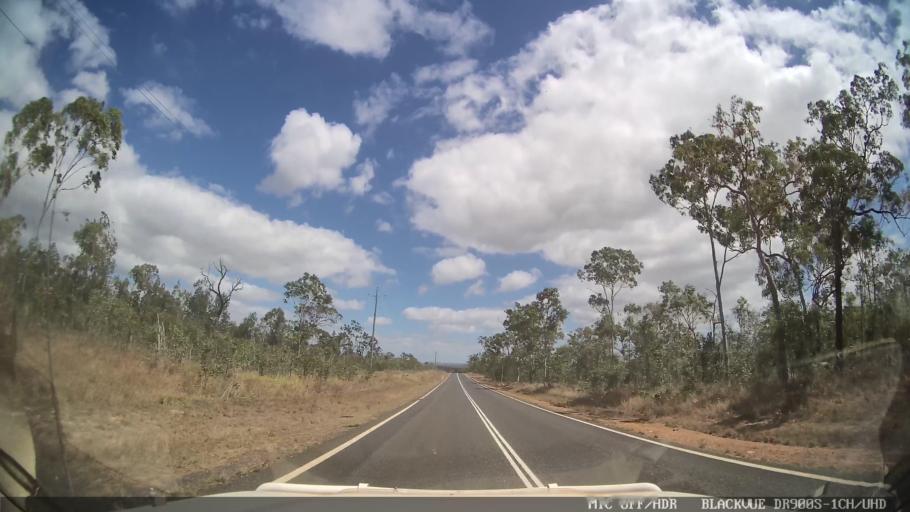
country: AU
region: Queensland
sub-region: Tablelands
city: Ravenshoe
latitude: -17.7310
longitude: 145.0436
